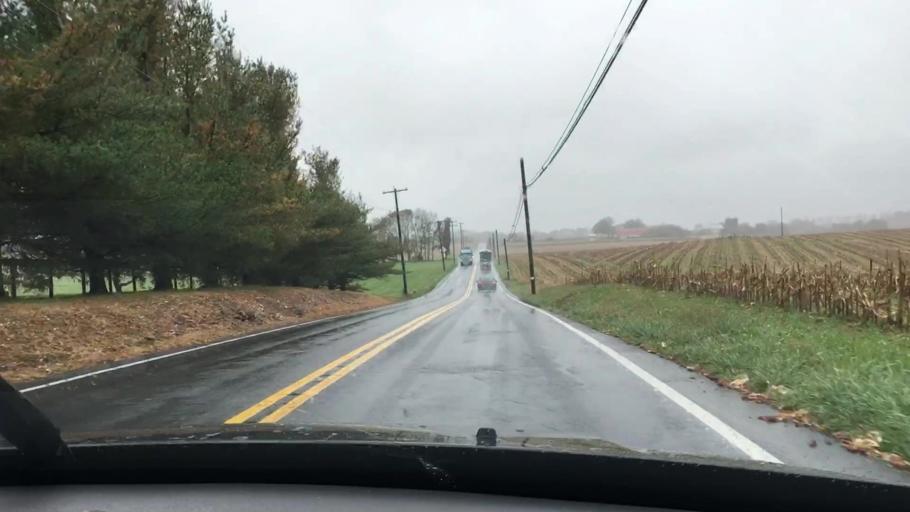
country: US
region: Maryland
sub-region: Frederick County
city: Adamstown
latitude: 39.2759
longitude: -77.4654
